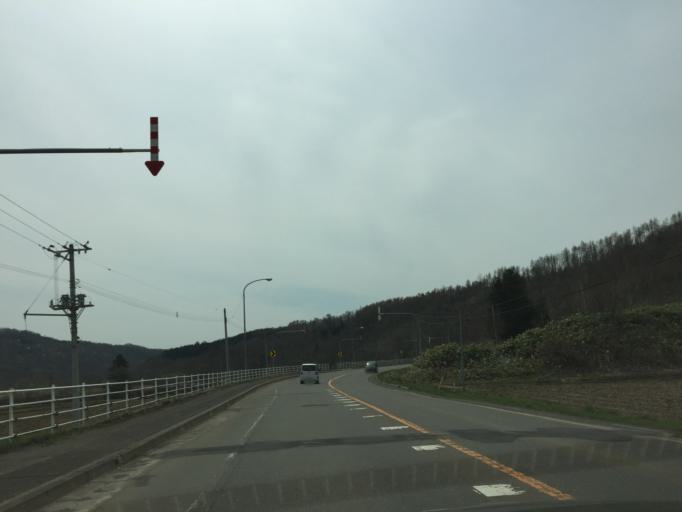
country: JP
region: Hokkaido
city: Ashibetsu
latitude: 43.5638
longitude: 142.1833
